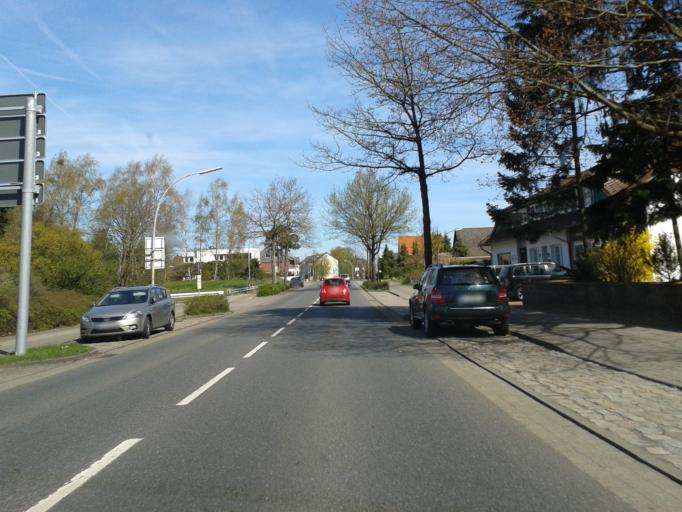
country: DE
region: Lower Saxony
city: Munster
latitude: 52.9831
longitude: 10.0868
